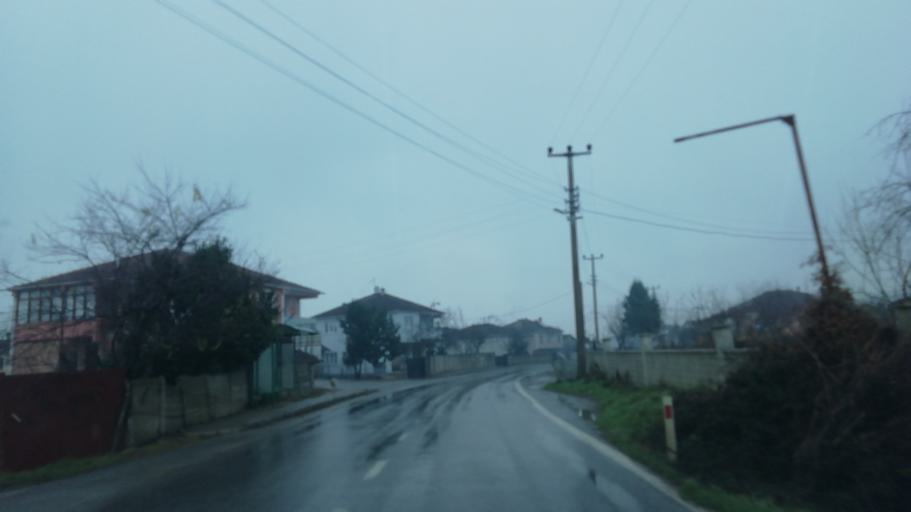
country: TR
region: Sakarya
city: Karapurcek
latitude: 40.6896
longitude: 30.4829
